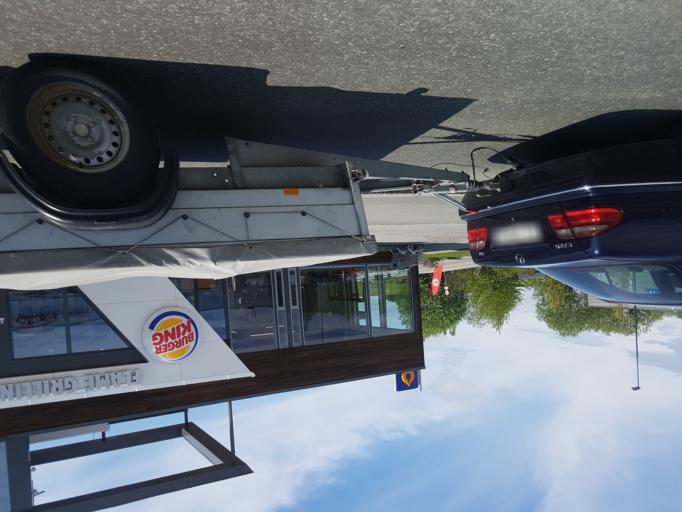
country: NO
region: Nord-Trondelag
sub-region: Levanger
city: Levanger
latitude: 63.7336
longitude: 11.2832
